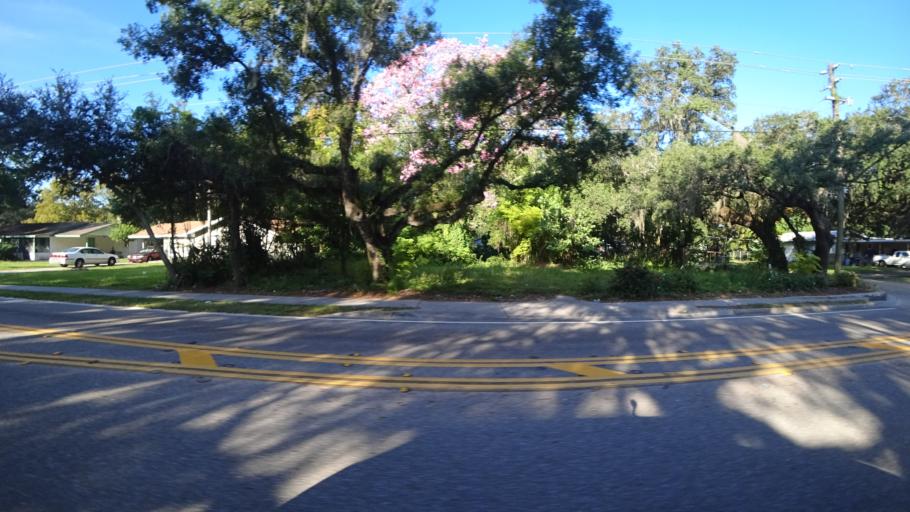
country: US
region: Florida
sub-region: Manatee County
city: West Samoset
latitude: 27.4720
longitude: -82.5548
